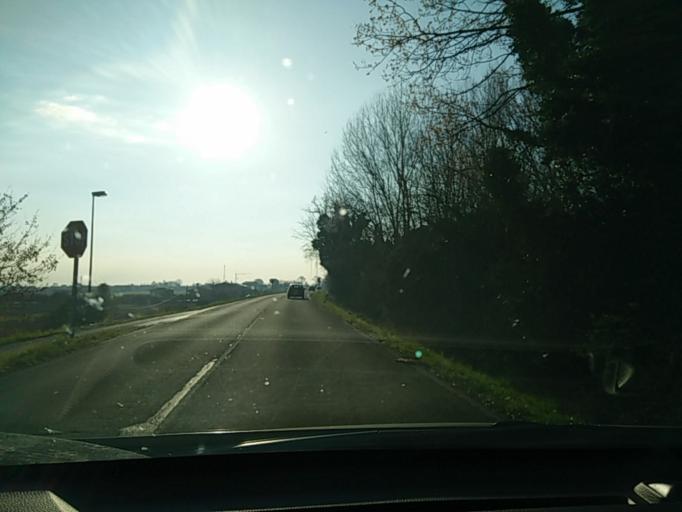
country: IT
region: Veneto
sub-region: Provincia di Venezia
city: Passarella
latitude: 45.5915
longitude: 12.6305
